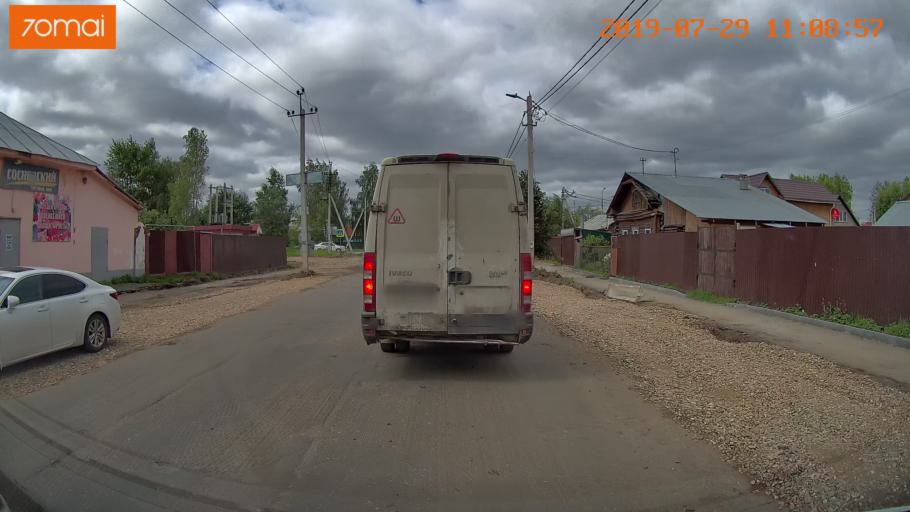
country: RU
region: Ivanovo
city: Bogorodskoye
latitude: 56.9953
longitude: 41.0316
